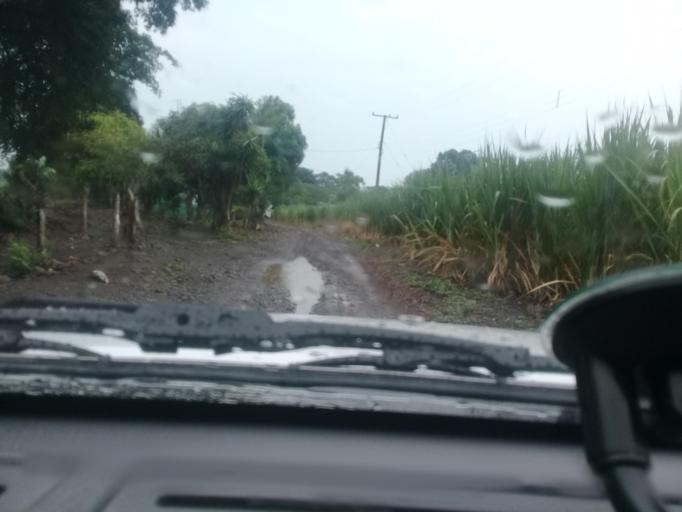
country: MX
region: Veracruz
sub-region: Puente Nacional
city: Cabezas
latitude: 19.3571
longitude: -96.3771
